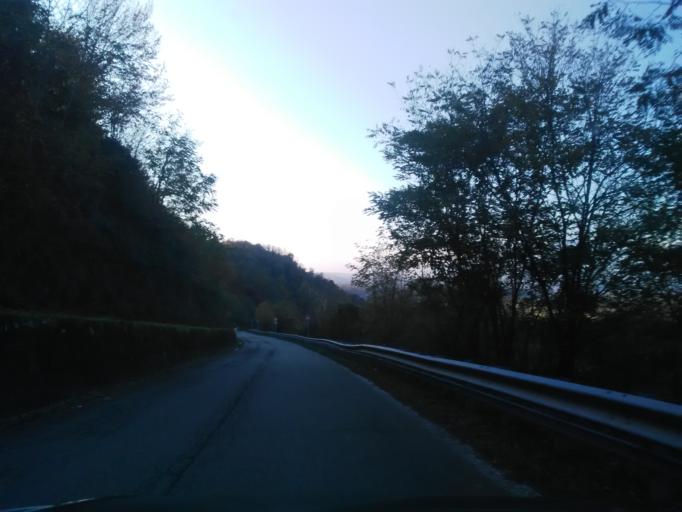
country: IT
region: Piedmont
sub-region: Provincia di Biella
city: Salussola
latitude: 45.4508
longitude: 8.1038
